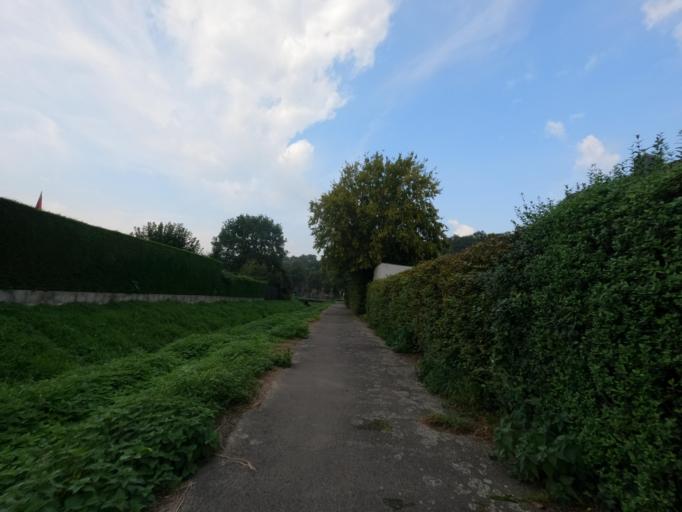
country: DE
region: North Rhine-Westphalia
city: Huckelhoven
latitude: 50.9985
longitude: 6.1913
